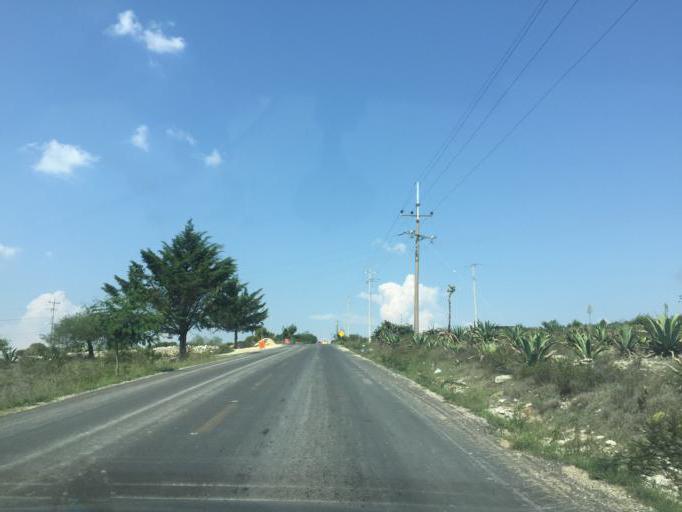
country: MX
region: Hidalgo
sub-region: Cardonal
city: Pozuelos
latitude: 20.6157
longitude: -99.0682
